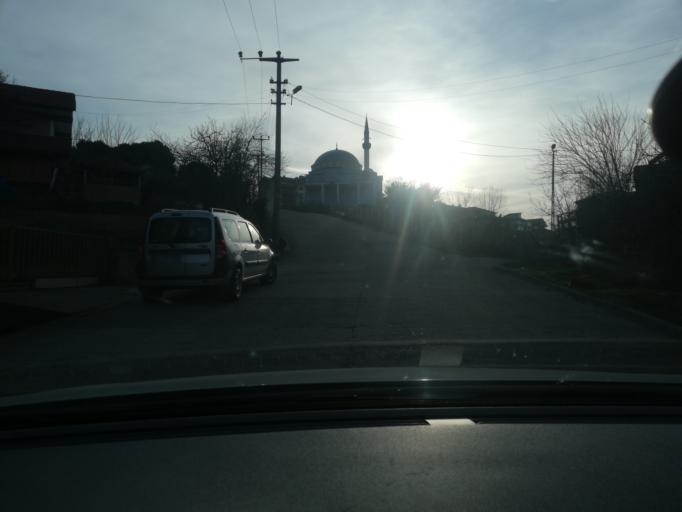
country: TR
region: Zonguldak
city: Tieum
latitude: 41.5586
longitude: 32.0292
